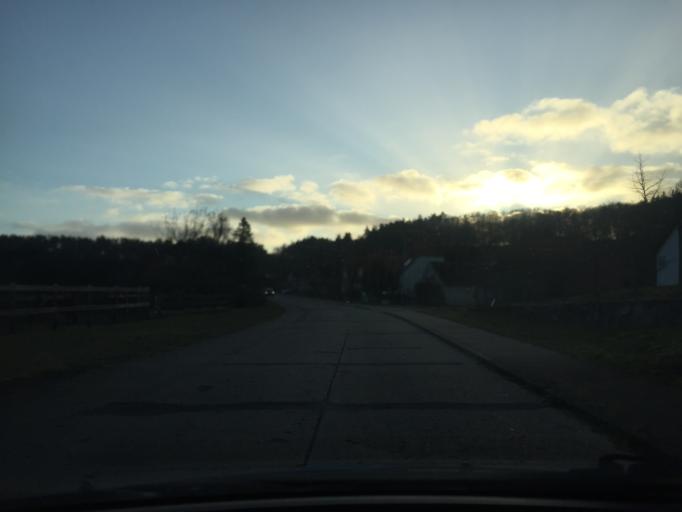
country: DE
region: Lower Saxony
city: Hitzacker
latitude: 53.1797
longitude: 10.9840
